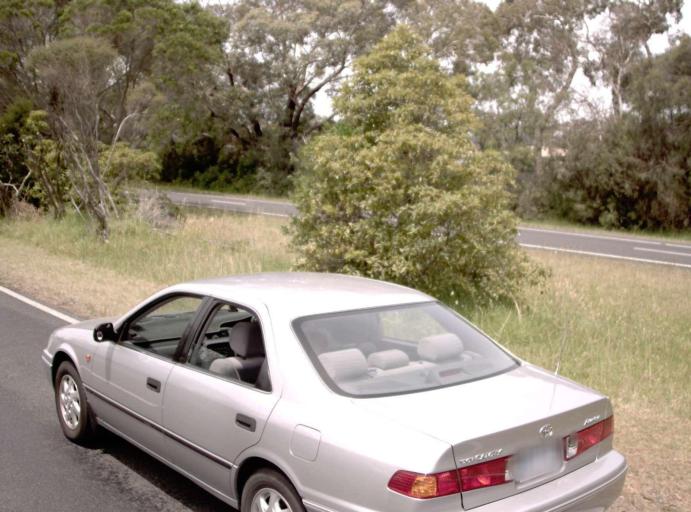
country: AU
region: Victoria
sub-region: Mornington Peninsula
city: Dromana
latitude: -38.3333
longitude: 144.9817
